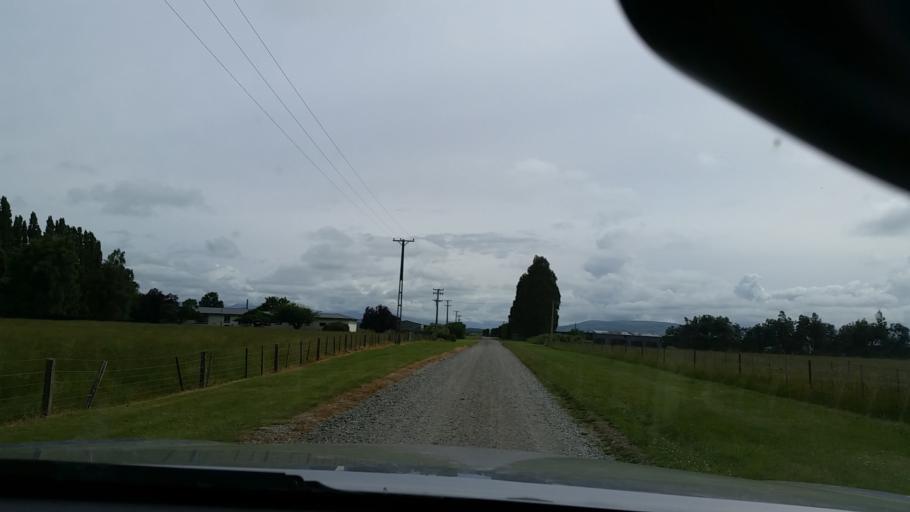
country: NZ
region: Southland
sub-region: Gore District
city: Gore
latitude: -45.8922
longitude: 168.7356
